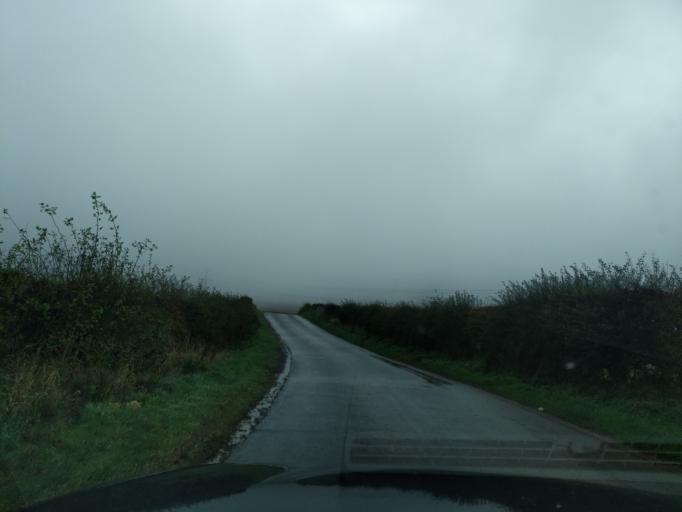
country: GB
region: Scotland
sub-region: East Lothian
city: Dunbar
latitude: 55.9438
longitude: -2.4043
